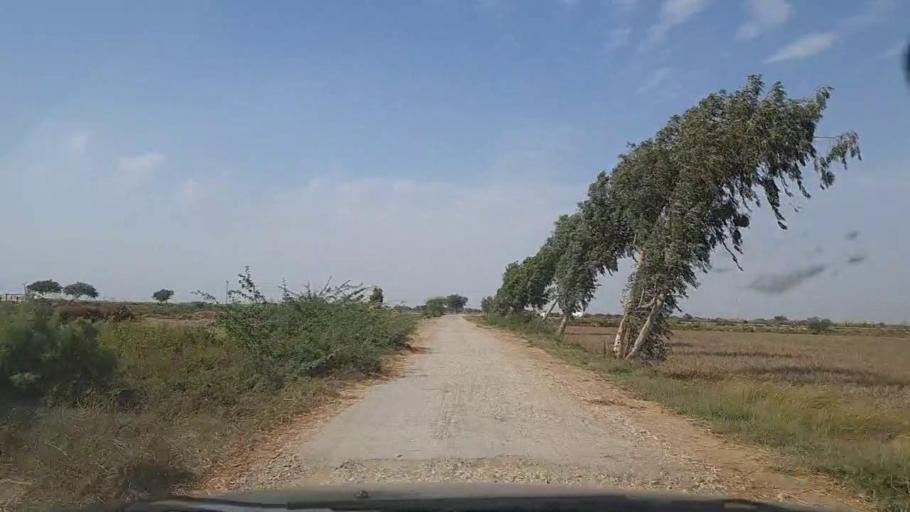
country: PK
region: Sindh
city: Mirpur Batoro
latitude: 24.5939
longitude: 68.2077
